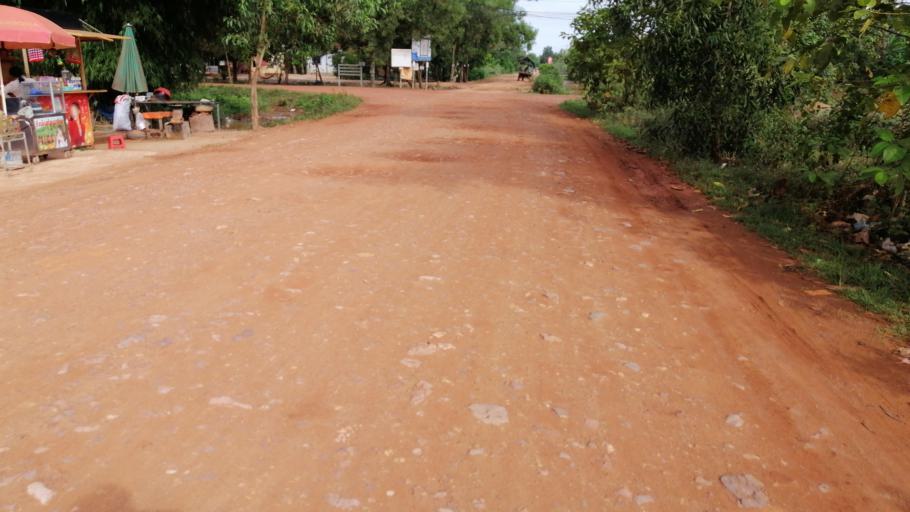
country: KH
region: Siem Reap
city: Siem Reap
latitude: 13.3594
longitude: 103.8265
